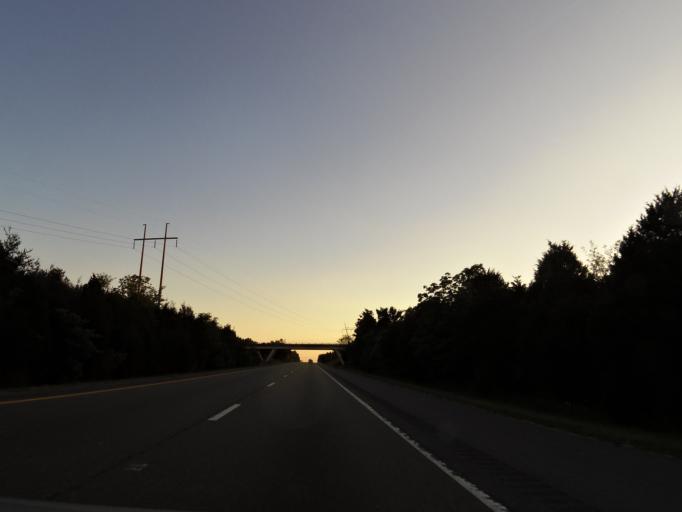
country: US
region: Tennessee
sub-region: Greene County
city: Mosheim
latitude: 36.2606
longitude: -82.9508
